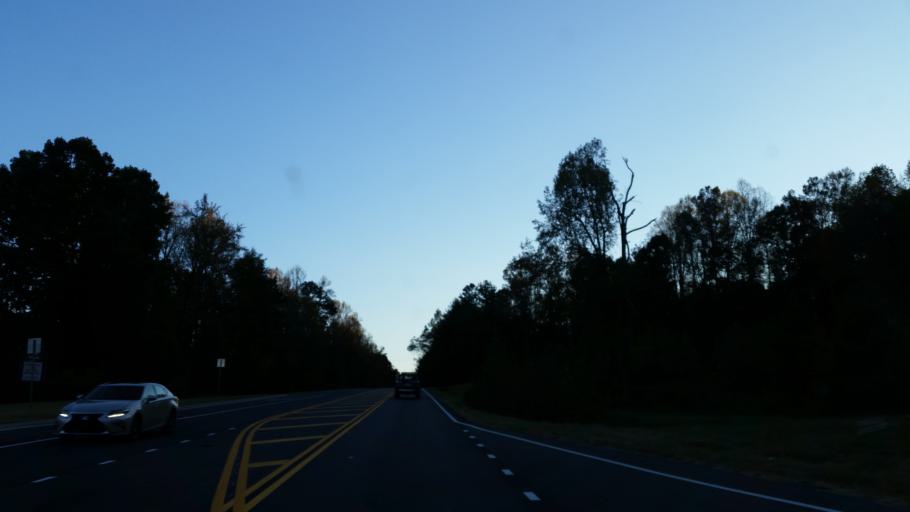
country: US
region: Georgia
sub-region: Lumpkin County
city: Dahlonega
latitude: 34.4962
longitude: -83.9704
